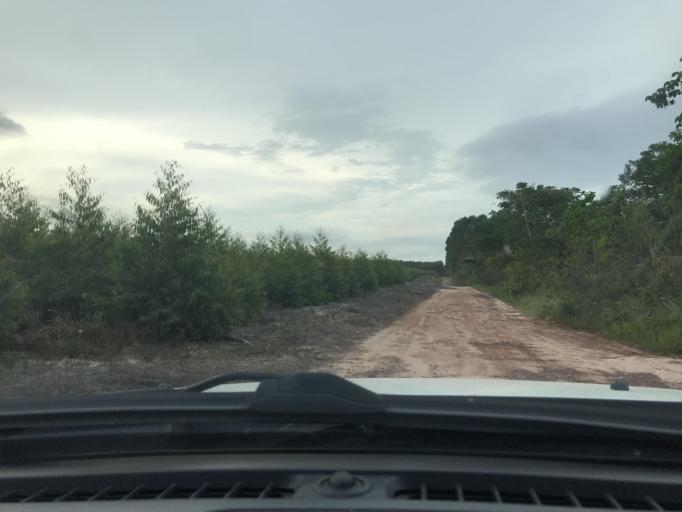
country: BR
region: Bahia
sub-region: Entre Rios
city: Entre Rios
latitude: -12.0863
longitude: -38.2045
